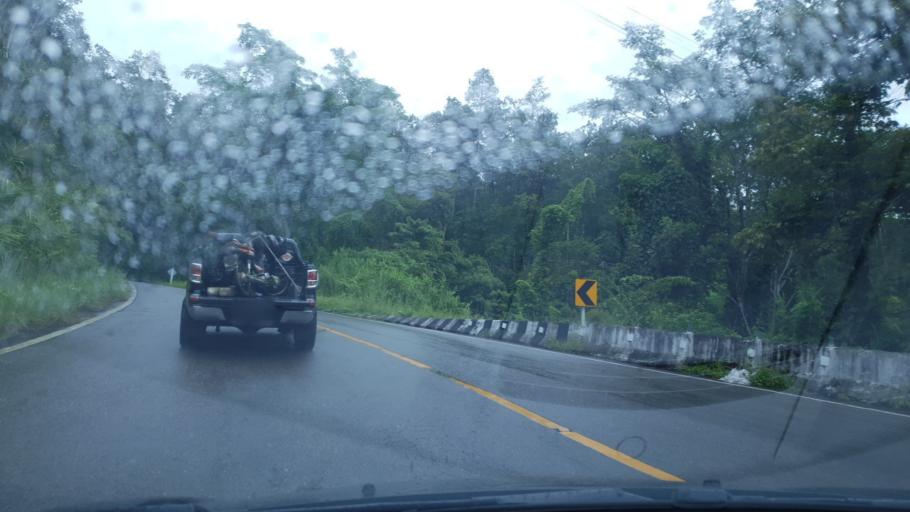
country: TH
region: Mae Hong Son
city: Mae La Noi
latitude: 18.5553
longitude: 97.9398
